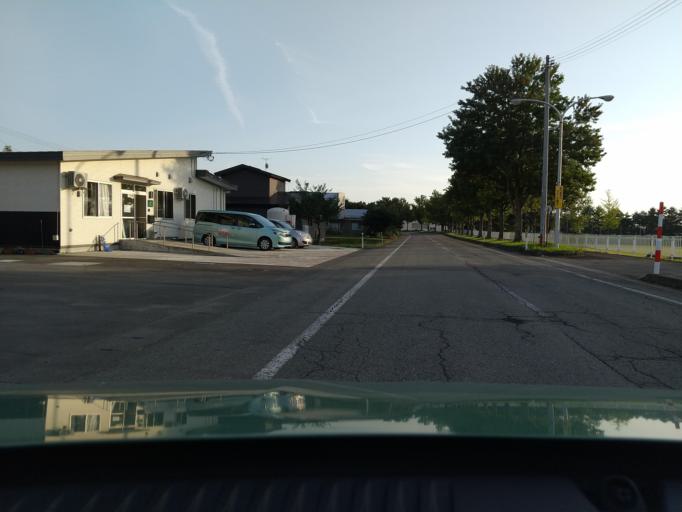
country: JP
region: Akita
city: Omagari
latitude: 39.4645
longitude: 140.5838
